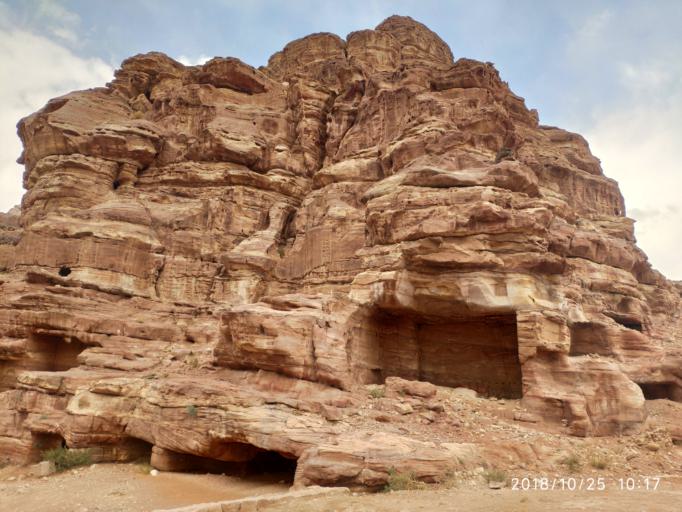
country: JO
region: Ma'an
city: Petra
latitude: 30.3310
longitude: 35.4396
